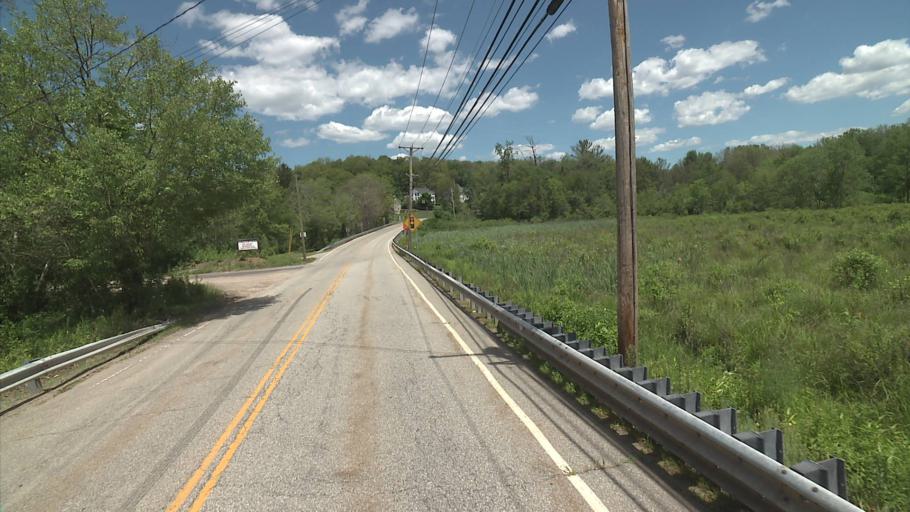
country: US
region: Connecticut
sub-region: Middlesex County
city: East Hampton
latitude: 41.5632
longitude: -72.5087
